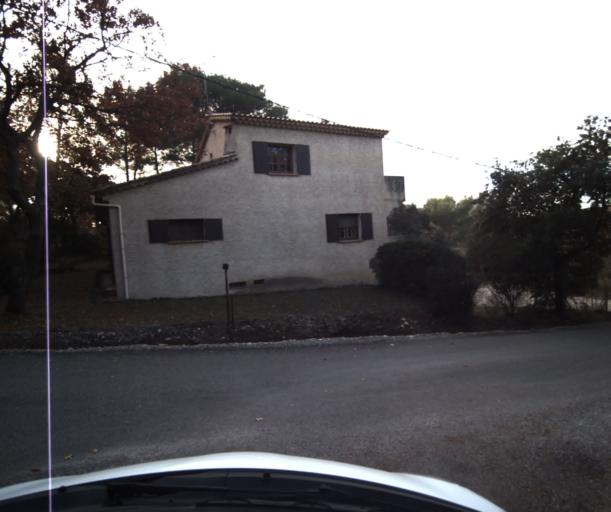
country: FR
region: Provence-Alpes-Cote d'Azur
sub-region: Departement du Vaucluse
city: Pertuis
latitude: 43.6937
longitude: 5.5357
